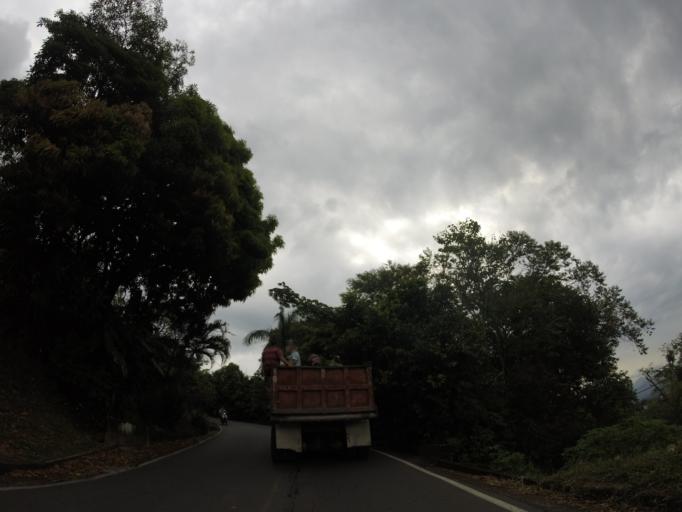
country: CO
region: Caldas
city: Victoria
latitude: 5.3203
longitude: -74.9136
